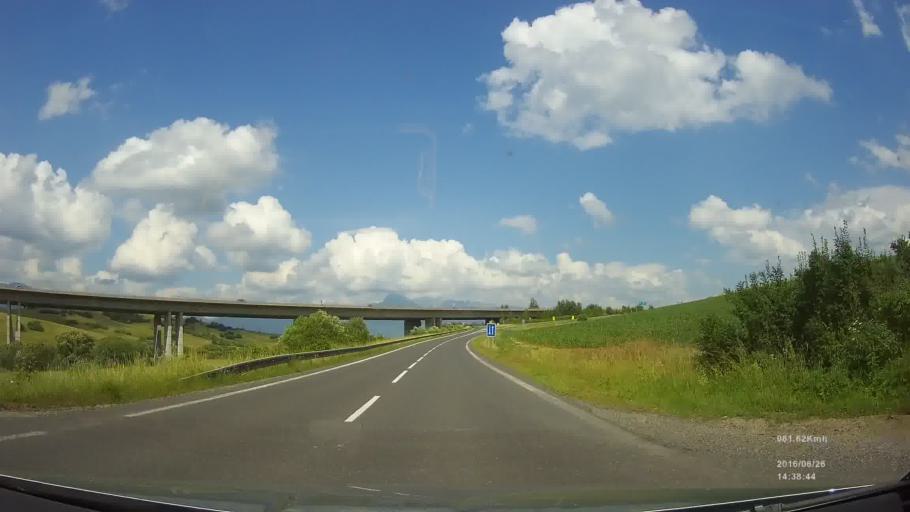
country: SK
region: Zilinsky
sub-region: Okres Liptovsky Mikulas
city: Hybe
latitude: 49.0537
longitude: 19.8454
